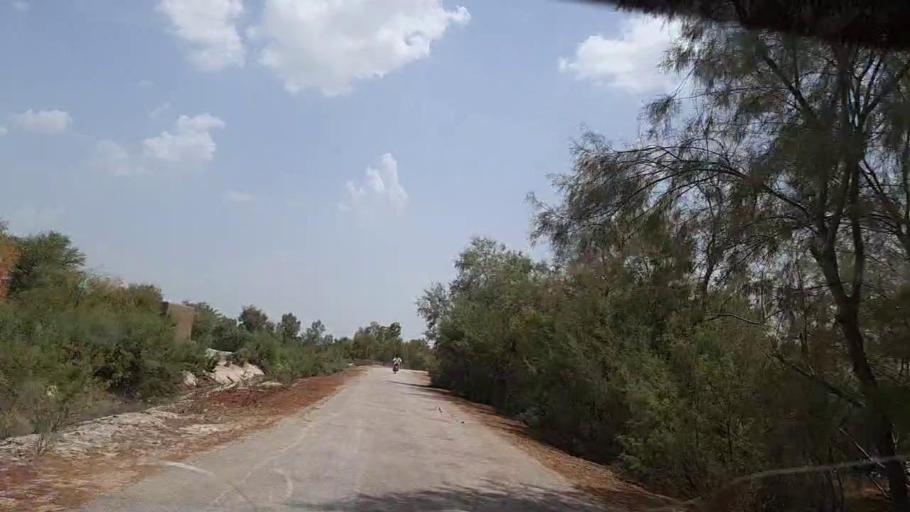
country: PK
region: Sindh
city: Bhan
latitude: 26.5086
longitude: 67.6405
